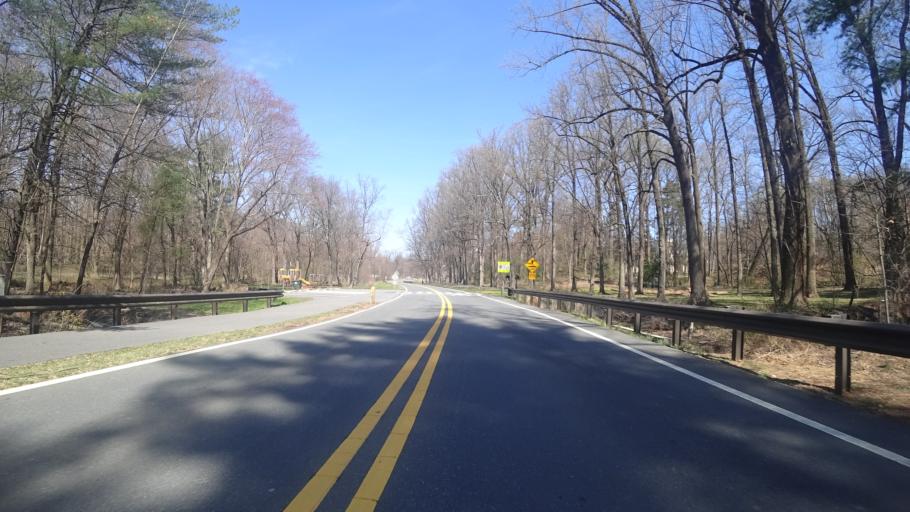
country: US
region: Maryland
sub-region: Montgomery County
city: Kemp Mill
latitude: 39.0340
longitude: -77.0293
